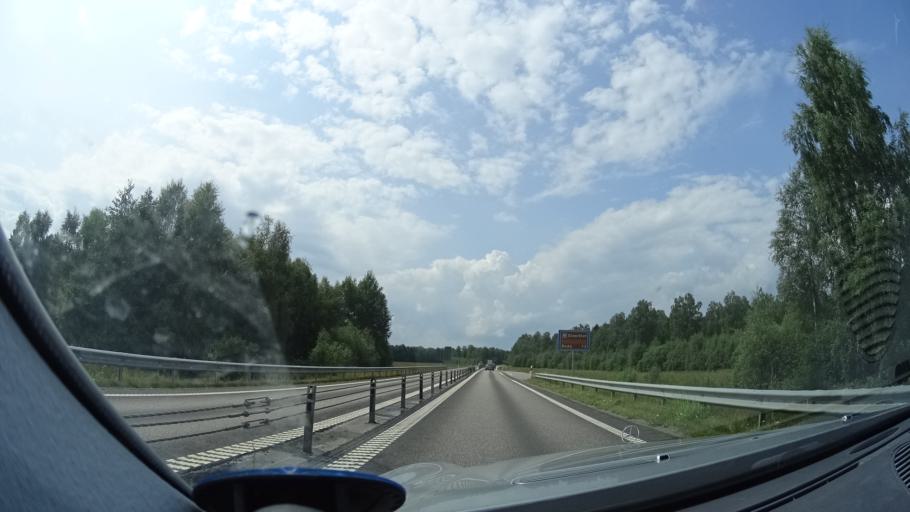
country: SE
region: Kalmar
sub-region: Nybro Kommun
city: Nybro
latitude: 56.7342
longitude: 15.8683
